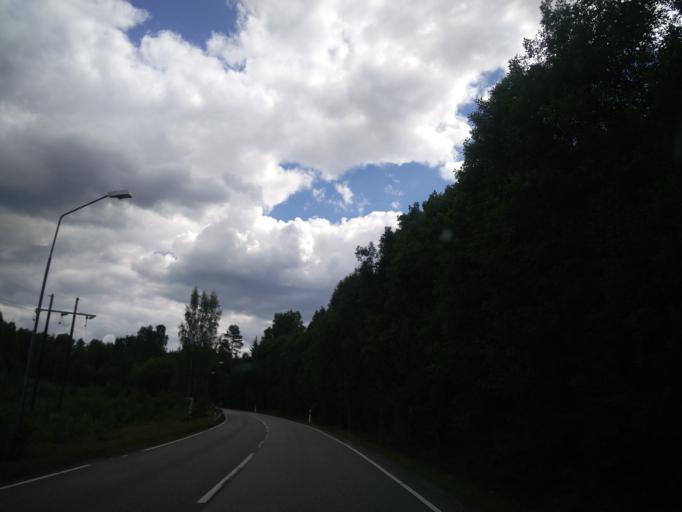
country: SE
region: OErebro
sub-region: Ljusnarsbergs Kommun
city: Kopparberg
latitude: 59.8702
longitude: 14.9928
